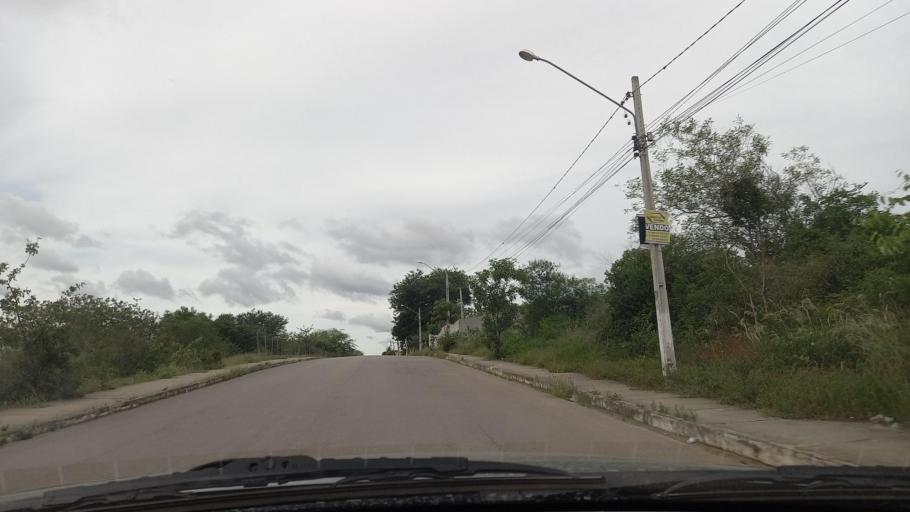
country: BR
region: Pernambuco
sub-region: Gravata
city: Gravata
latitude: -8.2141
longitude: -35.6053
